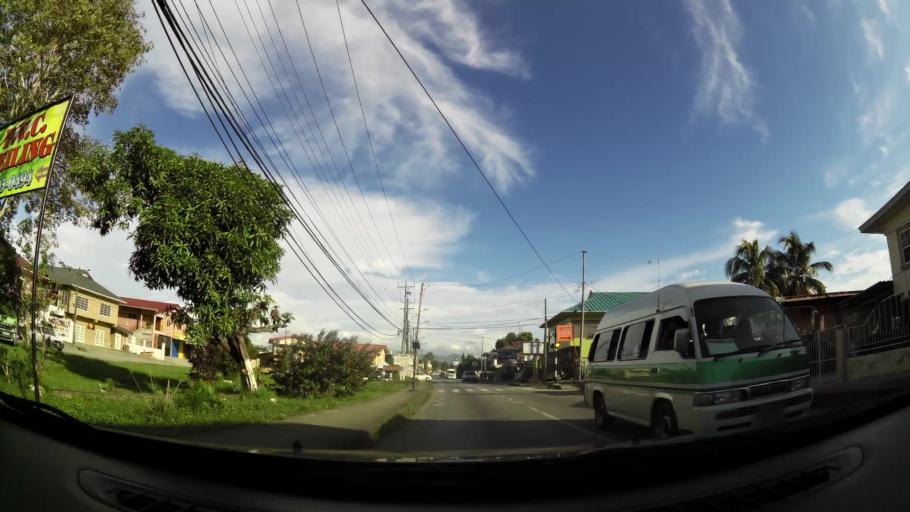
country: TT
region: Chaguanas
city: Chaguanas
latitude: 10.5619
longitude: -61.3732
